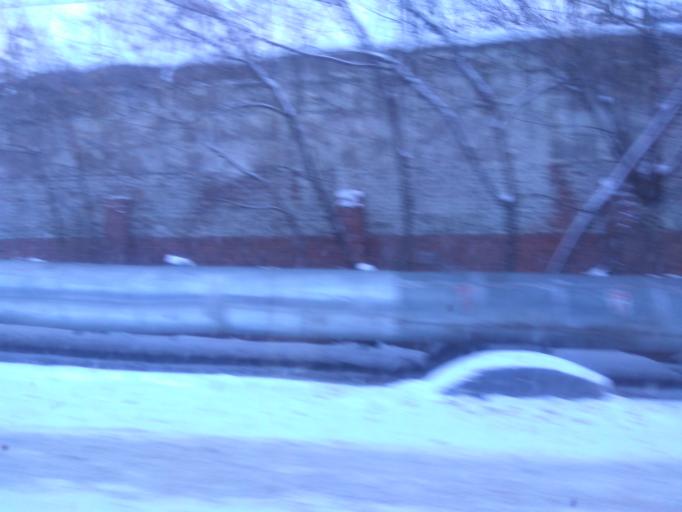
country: RU
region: Moscow
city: Taganskiy
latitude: 55.7284
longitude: 37.6938
